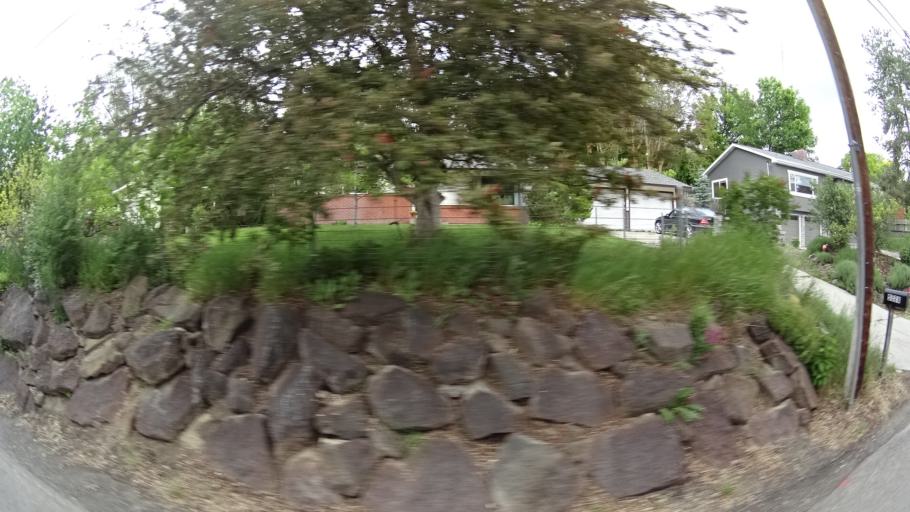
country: US
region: Idaho
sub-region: Ada County
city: Garden City
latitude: 43.6694
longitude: -116.2543
